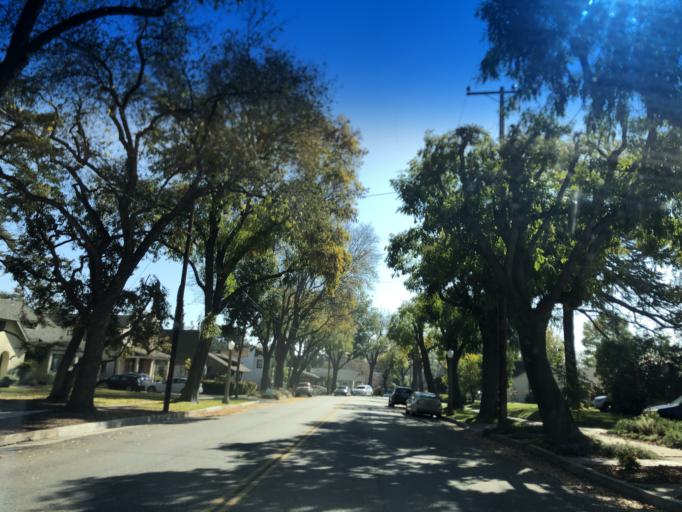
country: US
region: California
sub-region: Los Angeles County
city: South Pasadena
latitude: 34.1171
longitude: -118.1422
